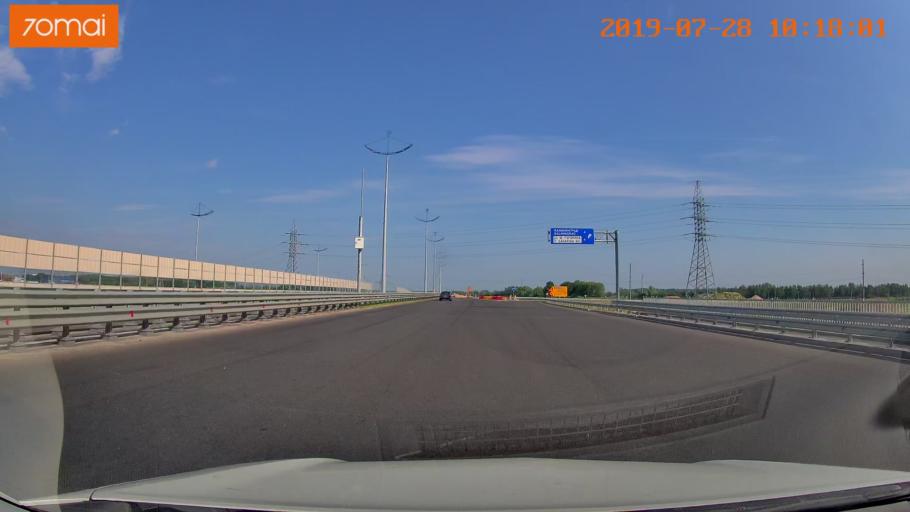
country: RU
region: Kaliningrad
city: Maloye Isakovo
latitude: 54.7462
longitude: 20.5916
